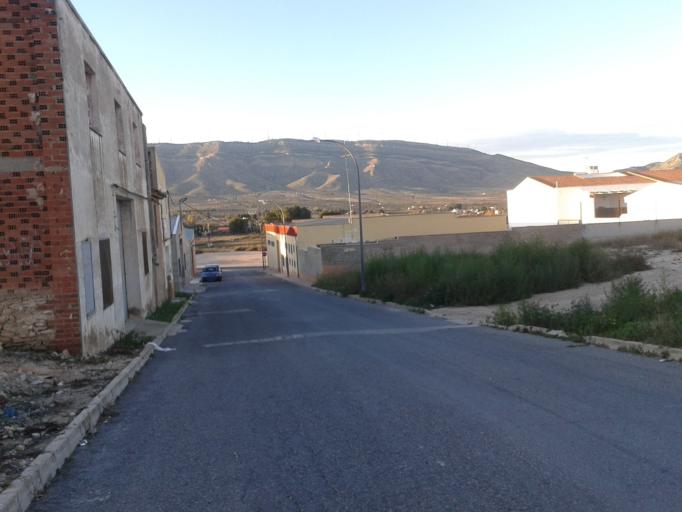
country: ES
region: Castille-La Mancha
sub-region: Provincia de Albacete
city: Caudete
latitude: 38.7057
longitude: -0.9925
